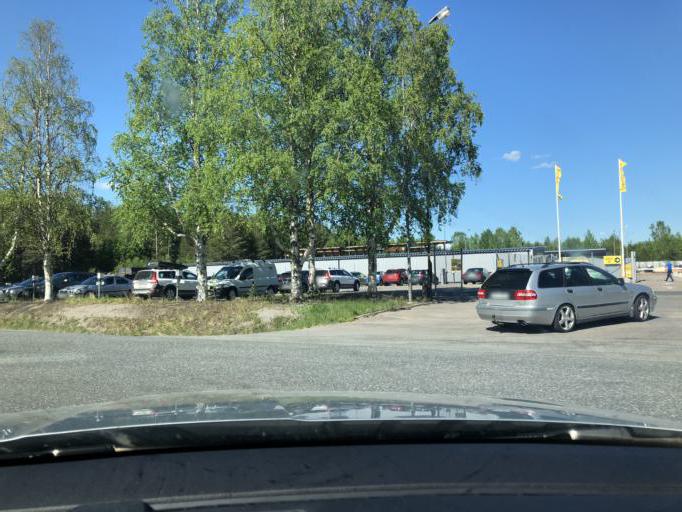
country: SE
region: Norrbotten
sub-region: Kalix Kommun
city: Kalix
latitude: 65.8531
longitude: 23.1867
